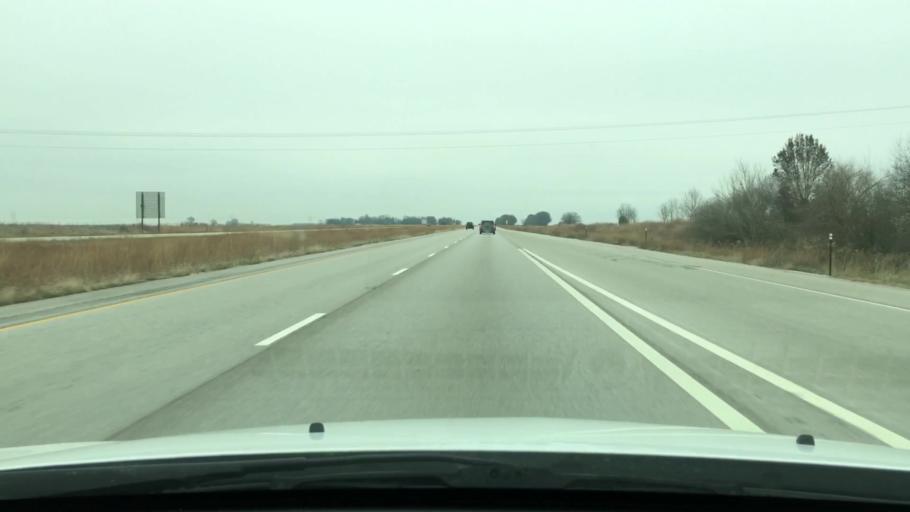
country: US
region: Illinois
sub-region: Sangamon County
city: New Berlin
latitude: 39.7369
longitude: -90.0364
